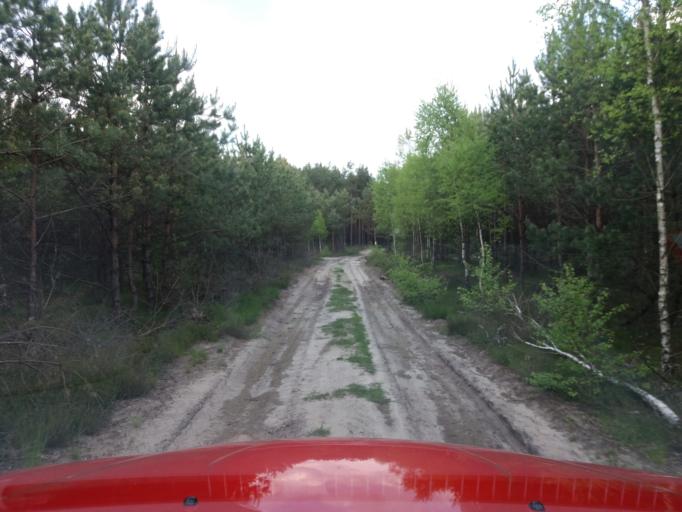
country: PL
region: West Pomeranian Voivodeship
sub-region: Powiat choszczenski
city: Drawno
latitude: 53.1253
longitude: 15.7602
